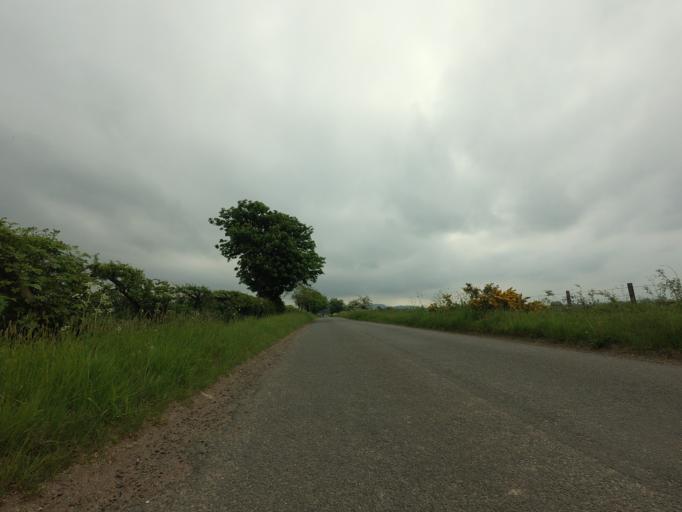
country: GB
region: Scotland
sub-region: Perth and Kinross
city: Kinross
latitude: 56.1922
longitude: -3.4337
